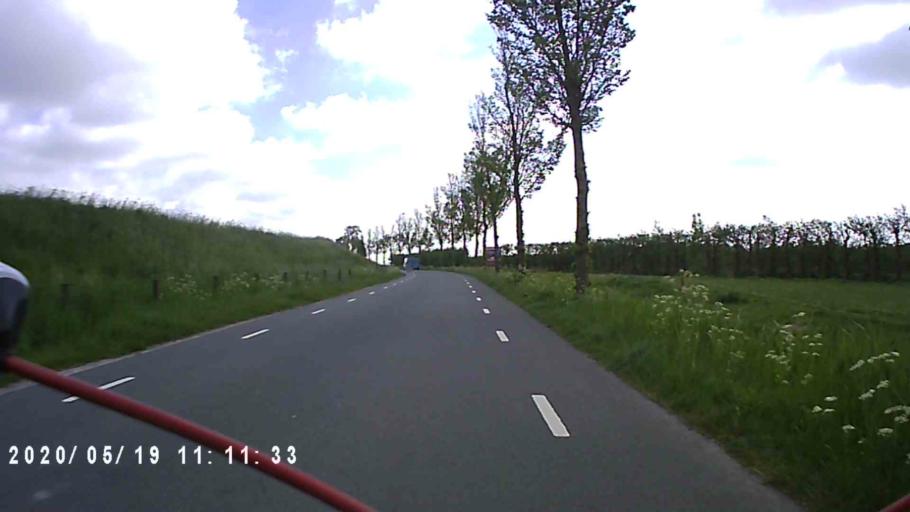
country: NL
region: Groningen
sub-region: Gemeente Zuidhorn
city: Grijpskerk
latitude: 53.2885
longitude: 6.3298
